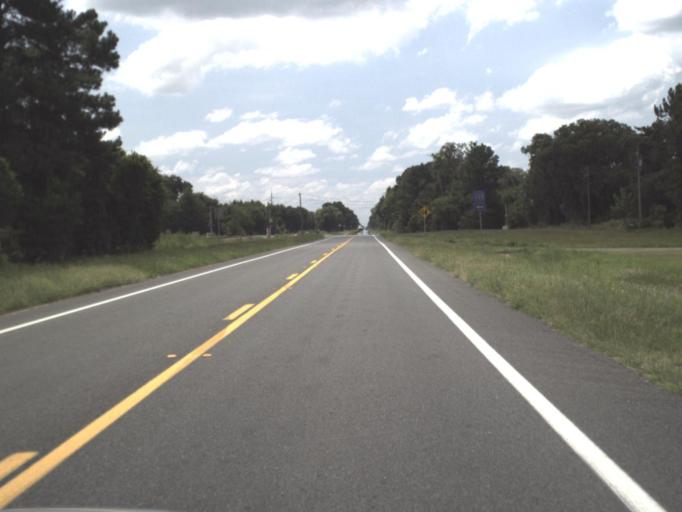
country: US
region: Florida
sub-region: Hamilton County
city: Jasper
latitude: 30.4717
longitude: -82.9081
